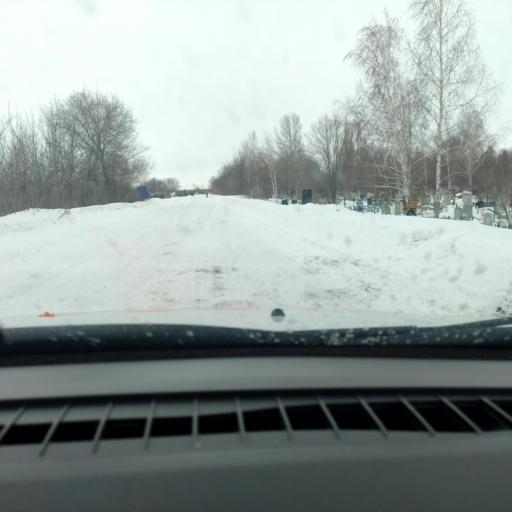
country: RU
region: Samara
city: Chapayevsk
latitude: 52.9919
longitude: 49.7426
